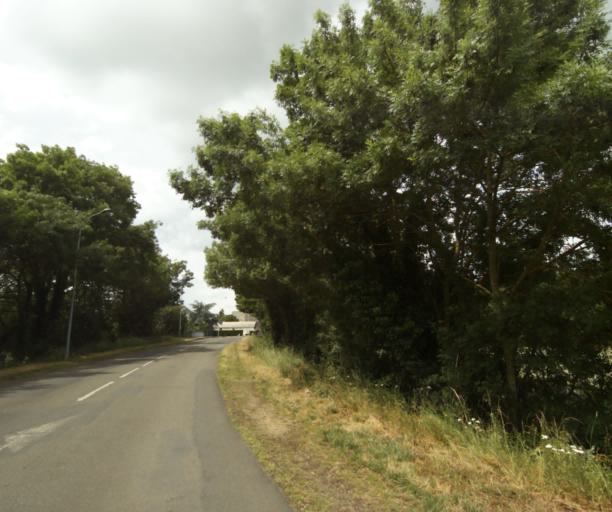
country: FR
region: Pays de la Loire
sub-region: Departement de la Sarthe
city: Sable-sur-Sarthe
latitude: 47.8352
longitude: -0.3376
